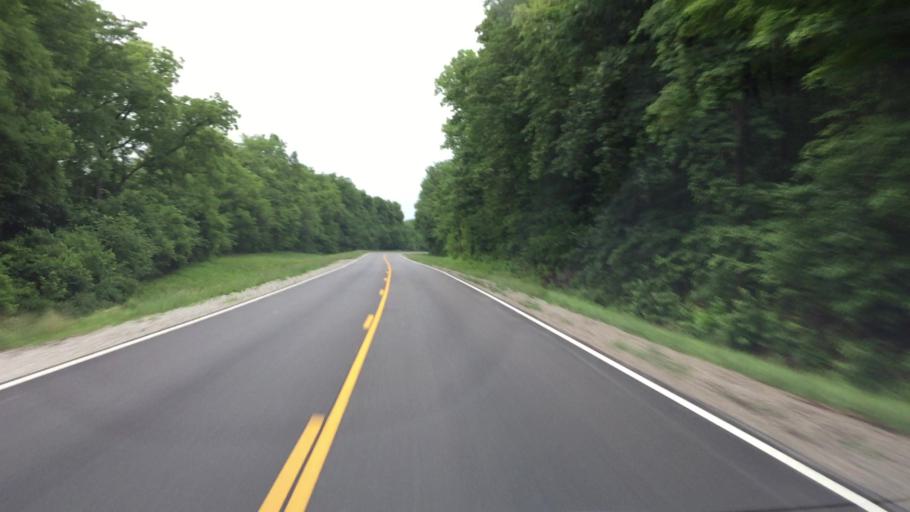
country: US
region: Iowa
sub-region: Lee County
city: Keokuk
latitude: 40.3725
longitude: -91.3931
